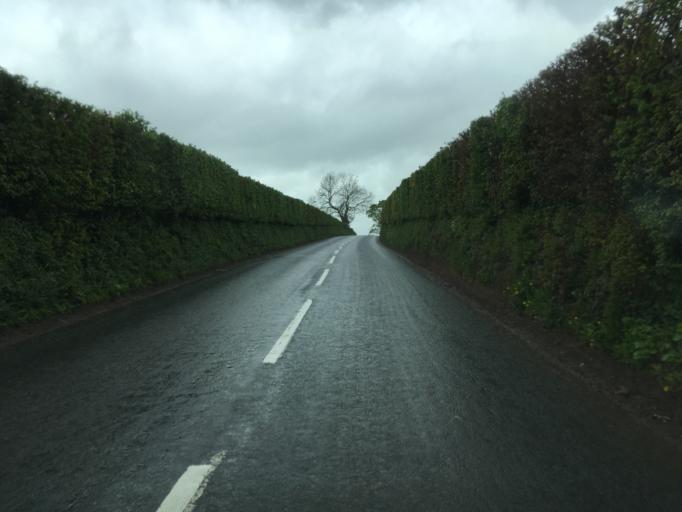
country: GB
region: England
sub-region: Bath and North East Somerset
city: East Harptree
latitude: 51.3118
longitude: -2.6292
